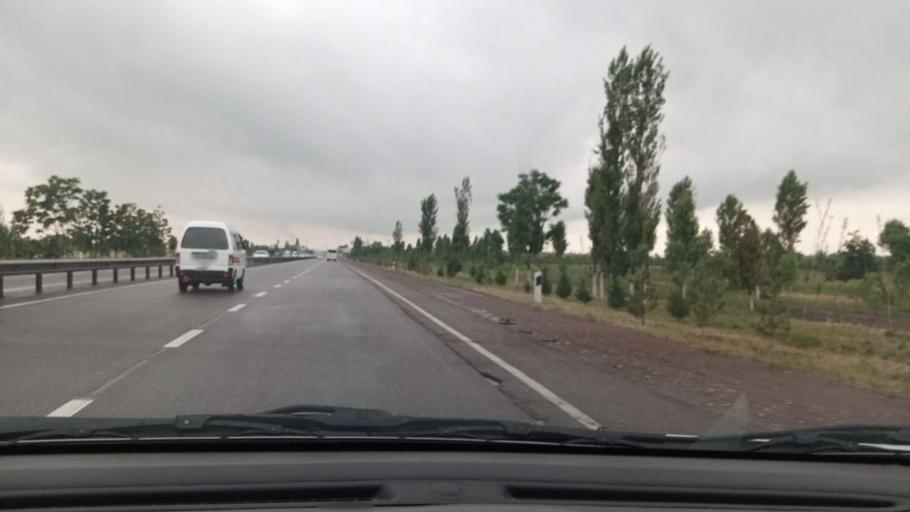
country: UZ
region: Toshkent
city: Ohangaron
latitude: 40.9160
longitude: 69.6061
